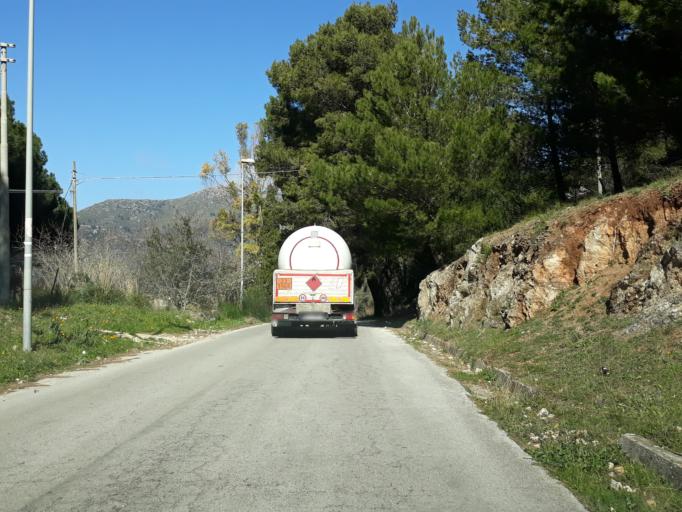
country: IT
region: Sicily
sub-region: Palermo
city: Piano dei Geli
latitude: 38.0825
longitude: 13.2709
